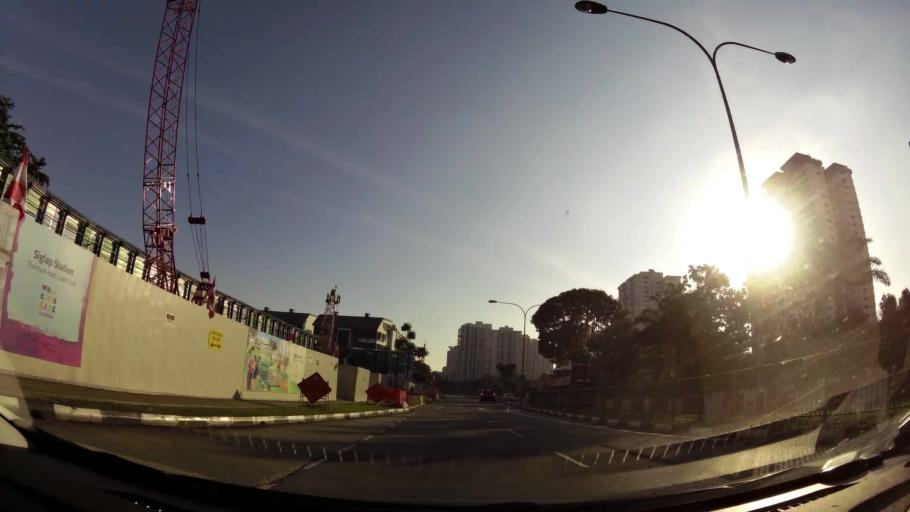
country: SG
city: Singapore
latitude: 1.3099
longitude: 103.9298
